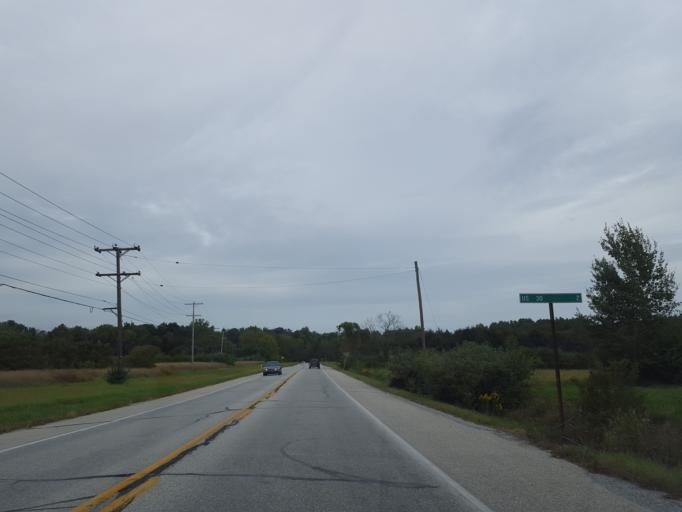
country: US
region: Pennsylvania
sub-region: York County
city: West York
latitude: 39.9164
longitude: -76.7955
